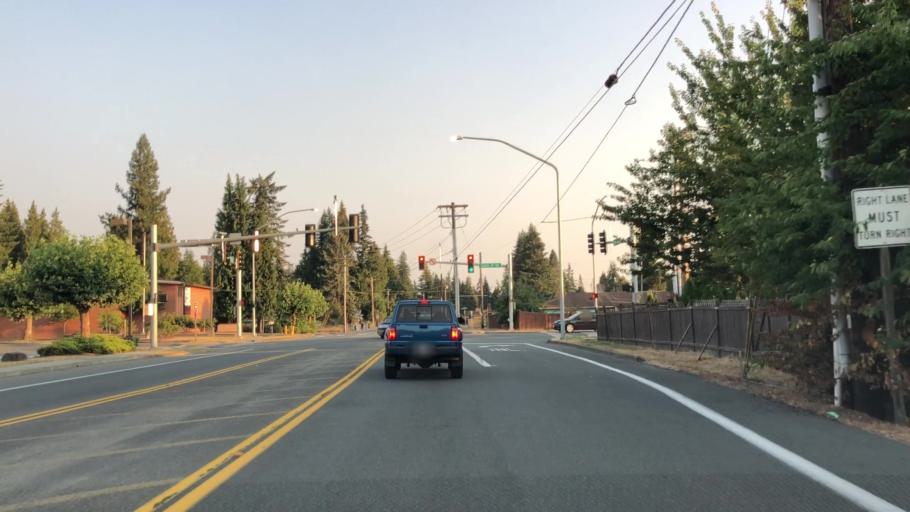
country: US
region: Washington
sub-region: Snohomish County
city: Smokey Point
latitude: 48.1191
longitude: -122.1625
